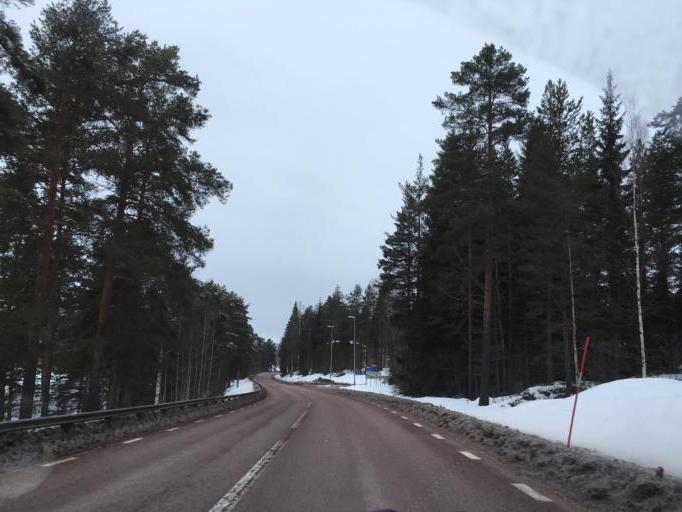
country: SE
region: Dalarna
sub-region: Alvdalens Kommun
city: AElvdalen
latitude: 61.2458
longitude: 14.0323
